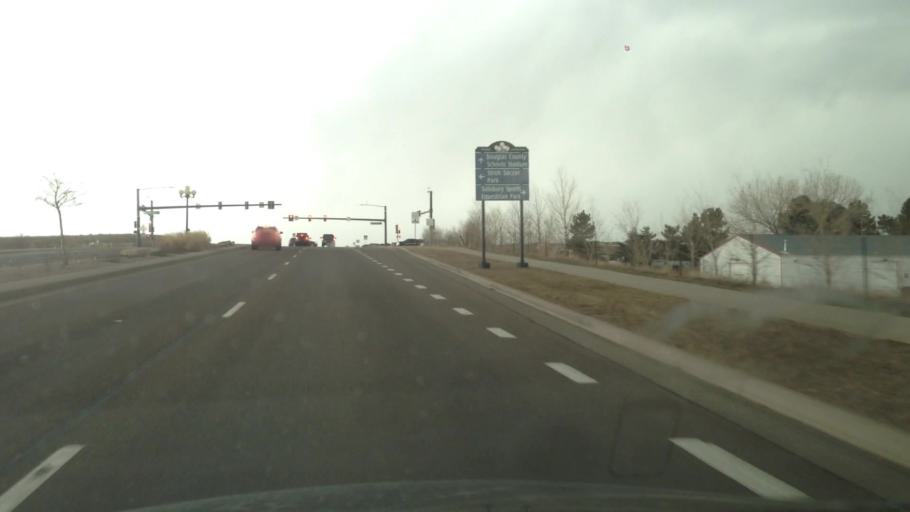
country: US
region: Colorado
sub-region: Douglas County
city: Parker
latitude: 39.4931
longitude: -104.7727
